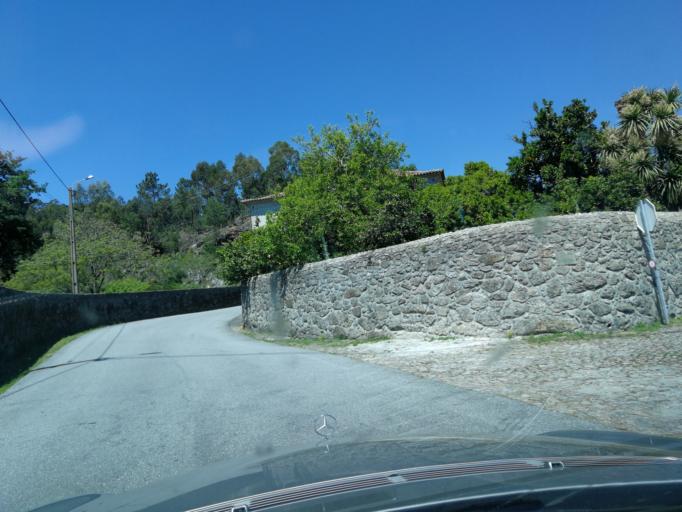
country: PT
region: Viana do Castelo
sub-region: Viana do Castelo
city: Meadela
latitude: 41.7363
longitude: -8.7854
